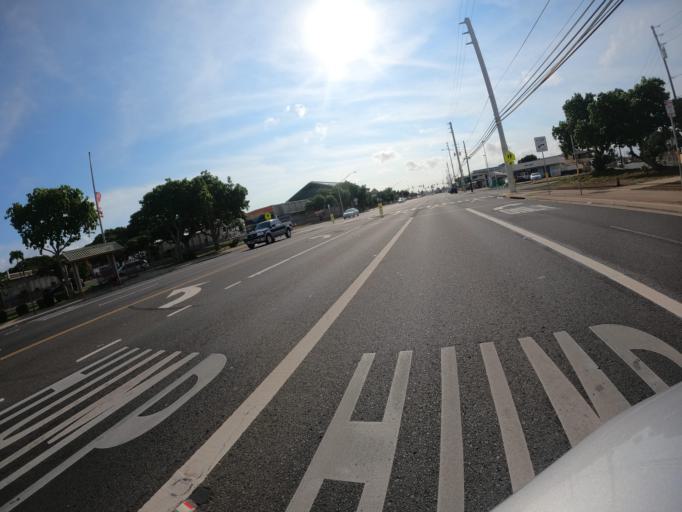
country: US
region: Hawaii
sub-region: Honolulu County
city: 'Ewa Beach
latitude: 21.3158
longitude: -158.0118
